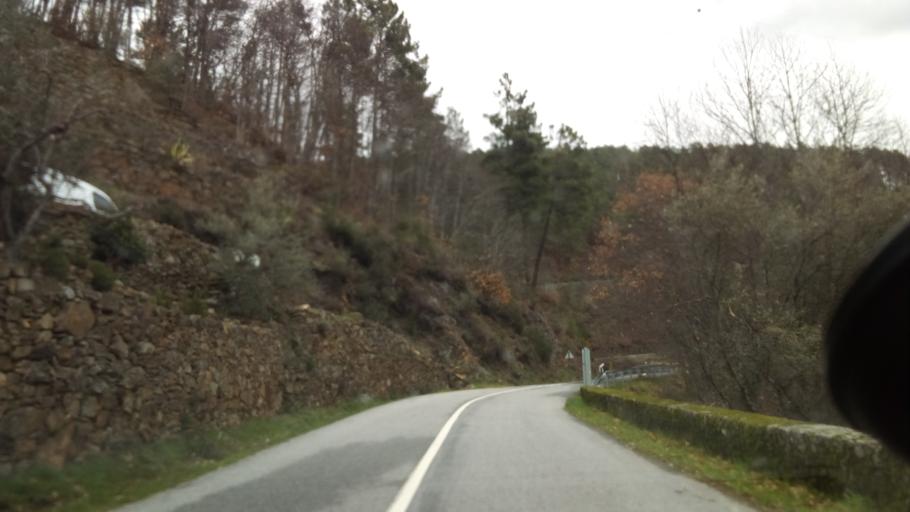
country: PT
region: Guarda
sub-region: Manteigas
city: Manteigas
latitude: 40.4112
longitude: -7.5285
